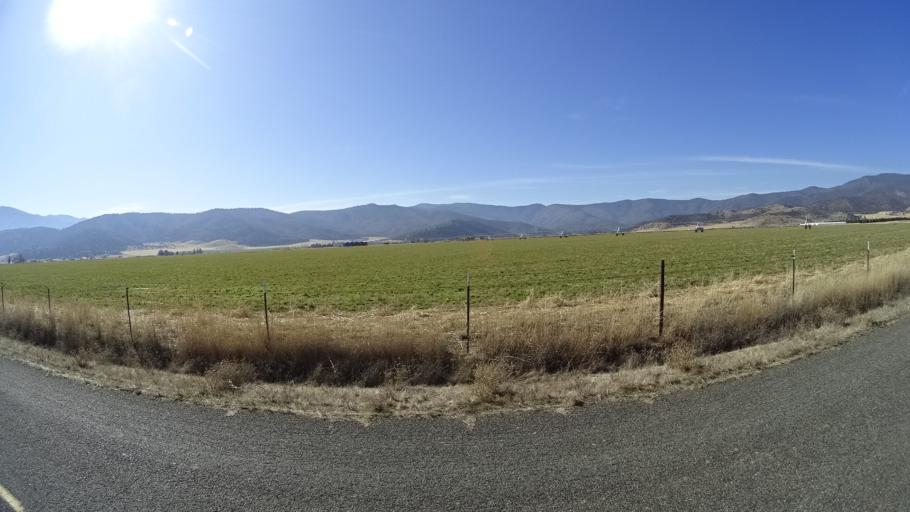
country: US
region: California
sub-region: Siskiyou County
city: Montague
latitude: 41.5481
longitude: -122.5421
